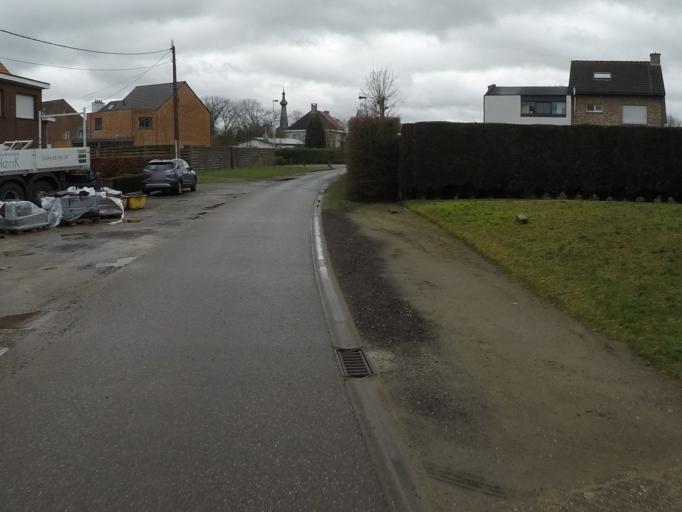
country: BE
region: Flanders
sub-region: Provincie Antwerpen
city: Schilde
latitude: 51.2146
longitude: 4.5946
